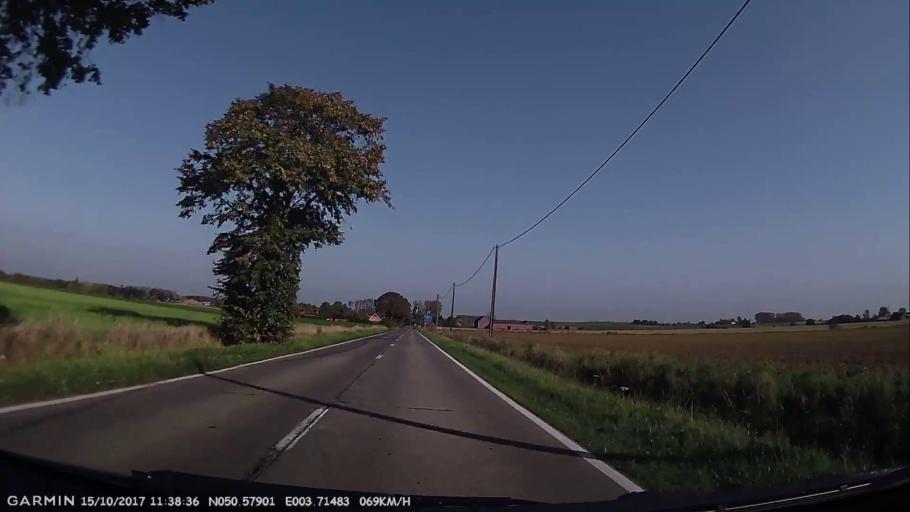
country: BE
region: Wallonia
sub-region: Province du Hainaut
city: Beloeil
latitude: 50.5792
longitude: 3.7150
